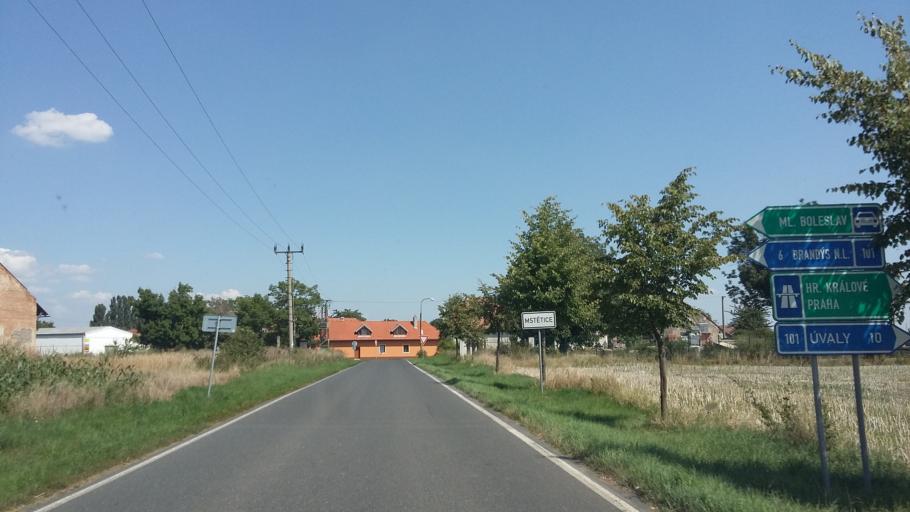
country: CZ
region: Central Bohemia
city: Jirny
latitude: 50.1415
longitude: 14.6908
